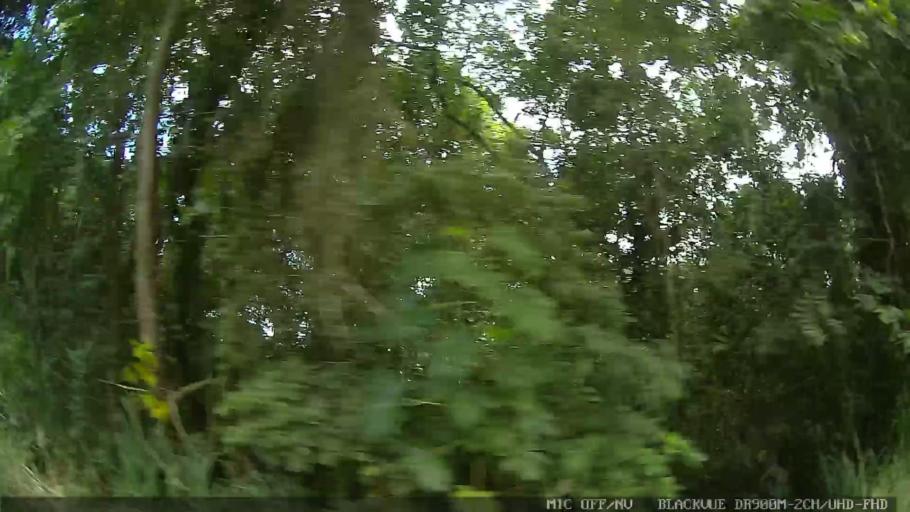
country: BR
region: Sao Paulo
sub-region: Iguape
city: Iguape
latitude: -24.6719
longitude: -47.4464
